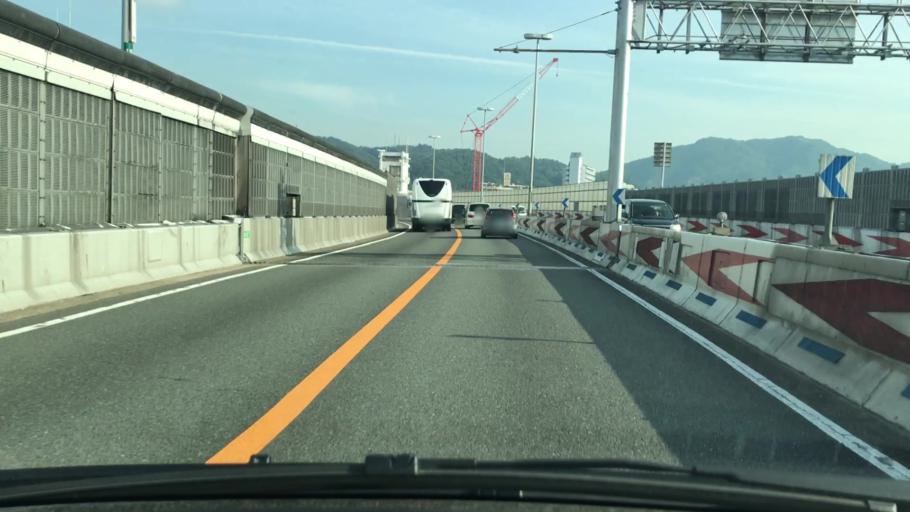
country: JP
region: Hyogo
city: Kobe
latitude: 34.6483
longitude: 135.1312
